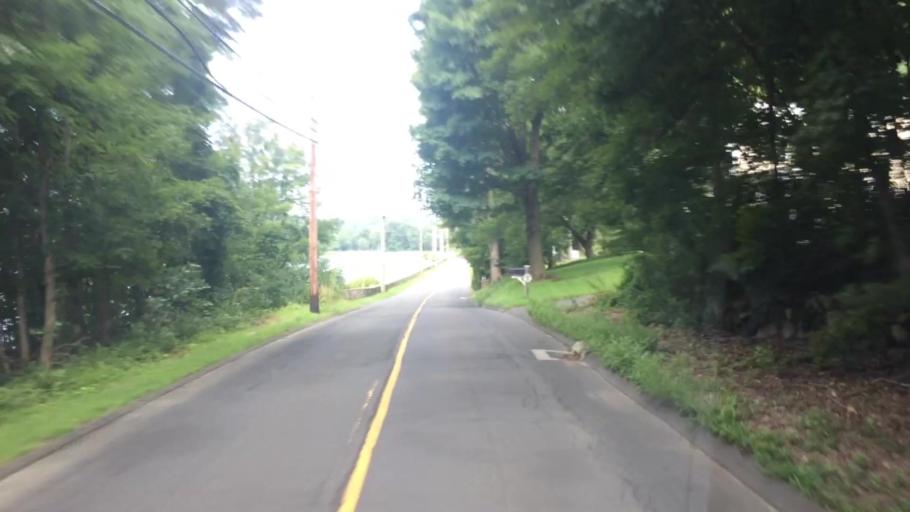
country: US
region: Connecticut
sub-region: Fairfield County
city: Danbury
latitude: 41.4099
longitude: -73.5031
